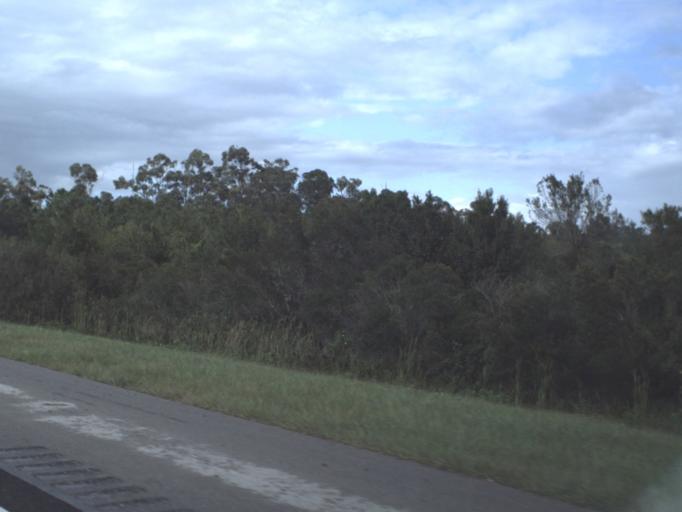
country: US
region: Florida
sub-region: Lee County
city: Suncoast Estates
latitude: 26.7687
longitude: -81.8775
